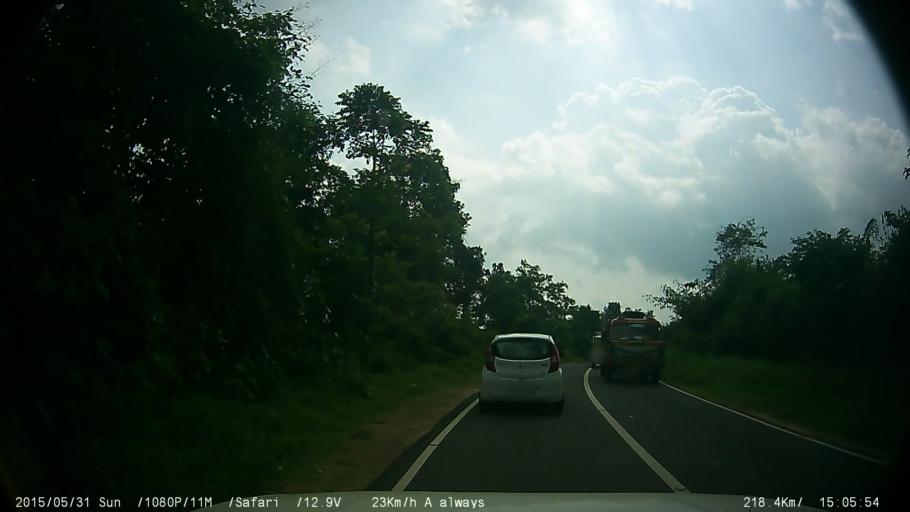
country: IN
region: Kerala
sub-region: Wayanad
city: Kalpetta
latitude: 11.6398
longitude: 76.2154
